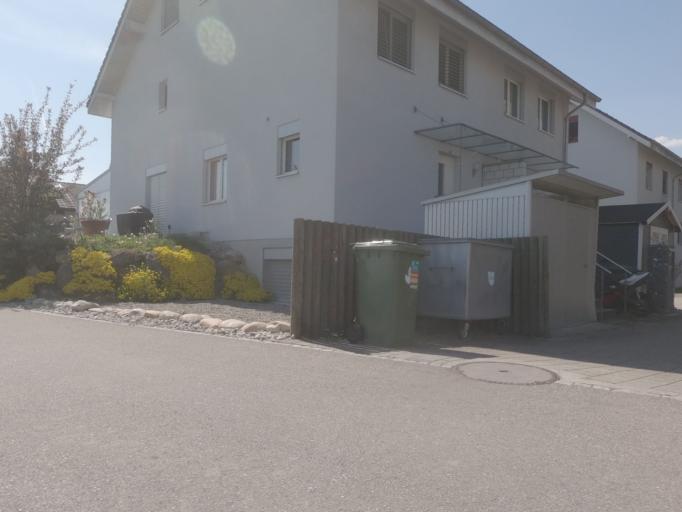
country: CH
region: Bern
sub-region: Biel/Bienne District
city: Orpund
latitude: 47.1171
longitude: 7.3399
